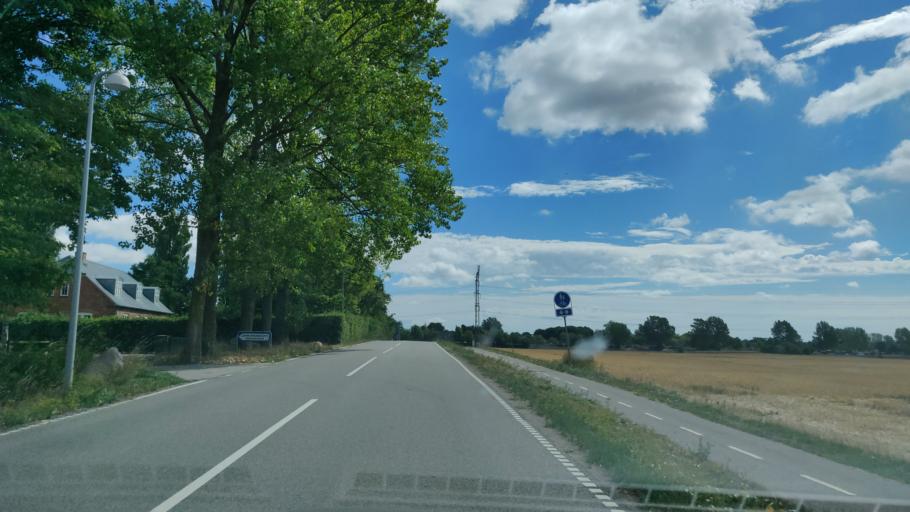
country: DK
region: Capital Region
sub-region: Hoje-Taastrup Kommune
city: Flong
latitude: 55.6622
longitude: 12.1704
